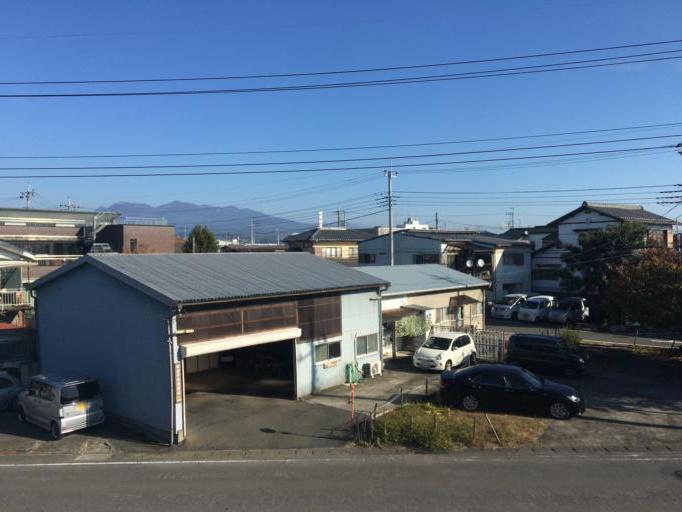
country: JP
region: Gunma
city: Maebashi-shi
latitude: 36.3792
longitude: 139.0954
